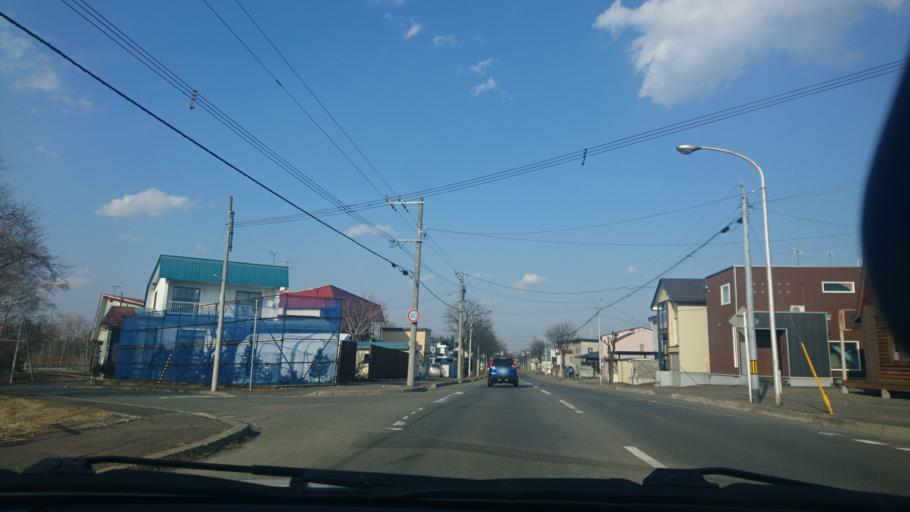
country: JP
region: Hokkaido
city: Obihiro
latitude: 42.9229
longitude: 143.1577
